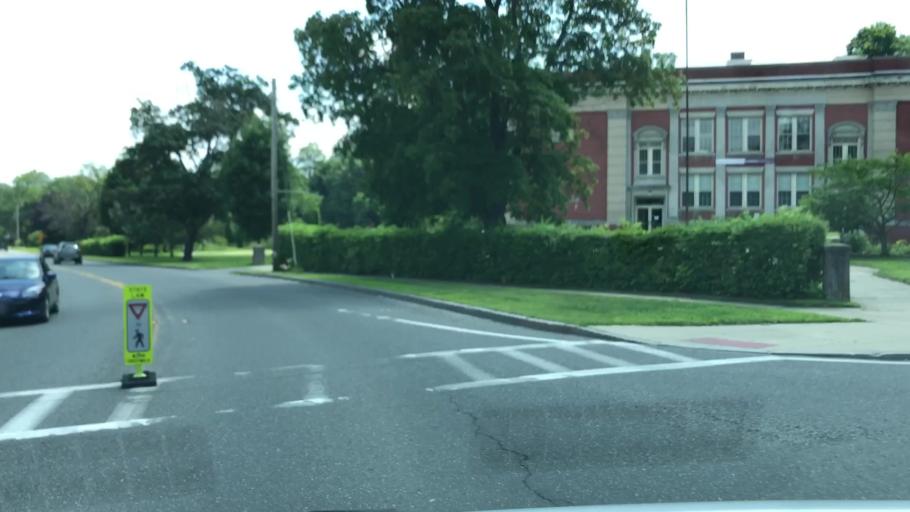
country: US
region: Massachusetts
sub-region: Hampshire County
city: Williamsburg
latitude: 42.3914
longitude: -72.7290
